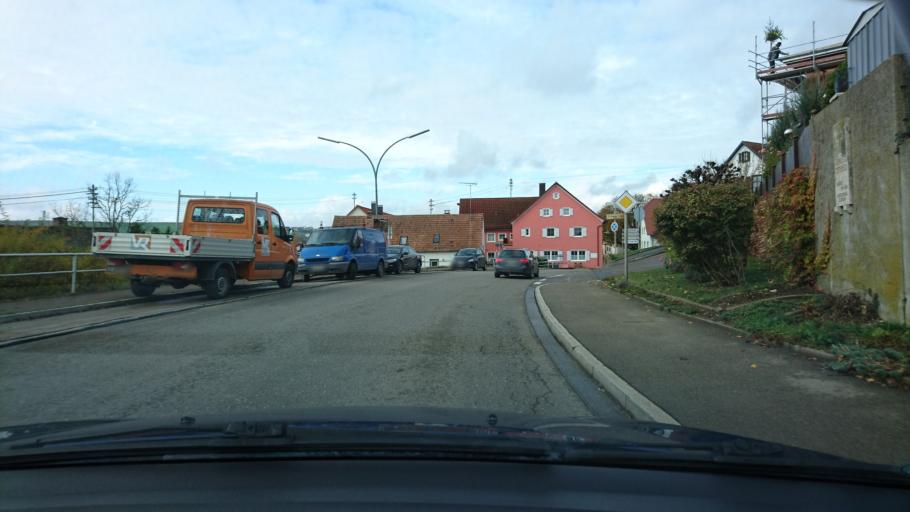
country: DE
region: Bavaria
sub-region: Swabia
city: Bissingen
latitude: 48.7131
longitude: 10.6213
